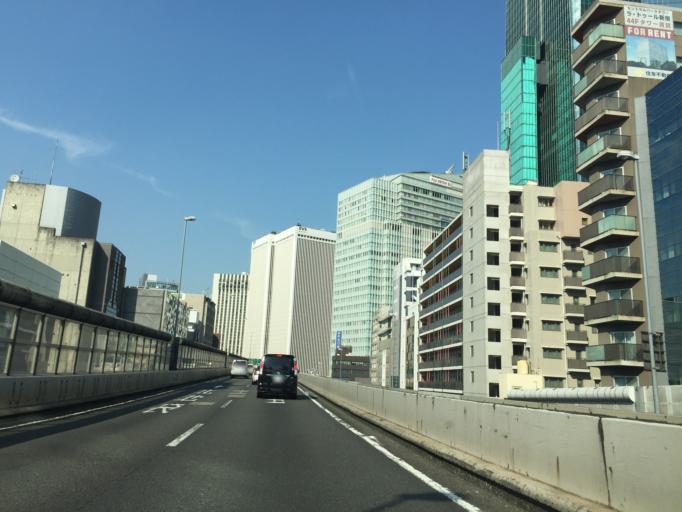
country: JP
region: Tokyo
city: Tokyo
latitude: 35.6646
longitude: 139.7348
